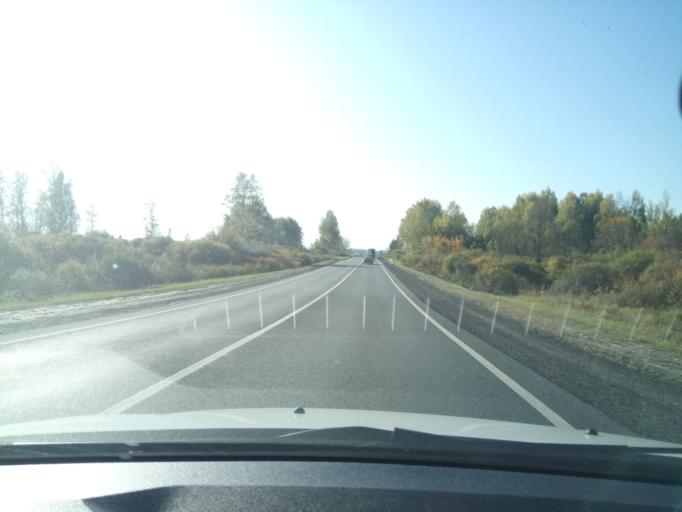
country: RU
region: Nizjnij Novgorod
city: Dal'neye Konstantinovo
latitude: 55.9695
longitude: 43.9737
